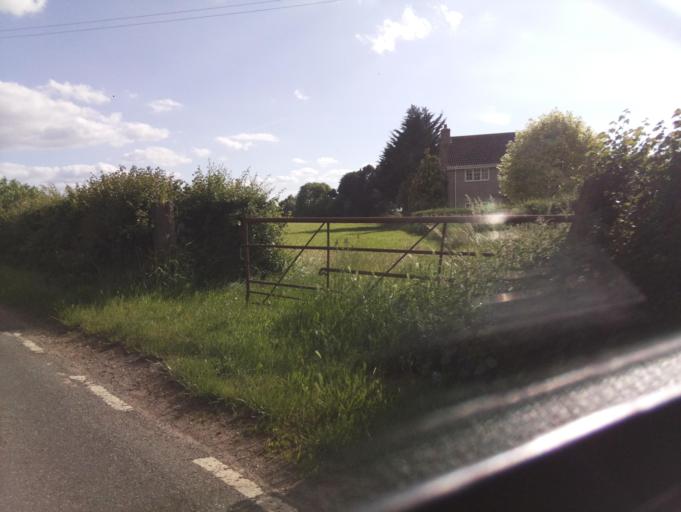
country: GB
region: England
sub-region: Somerset
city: Westonzoyland
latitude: 51.0936
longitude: -2.8775
